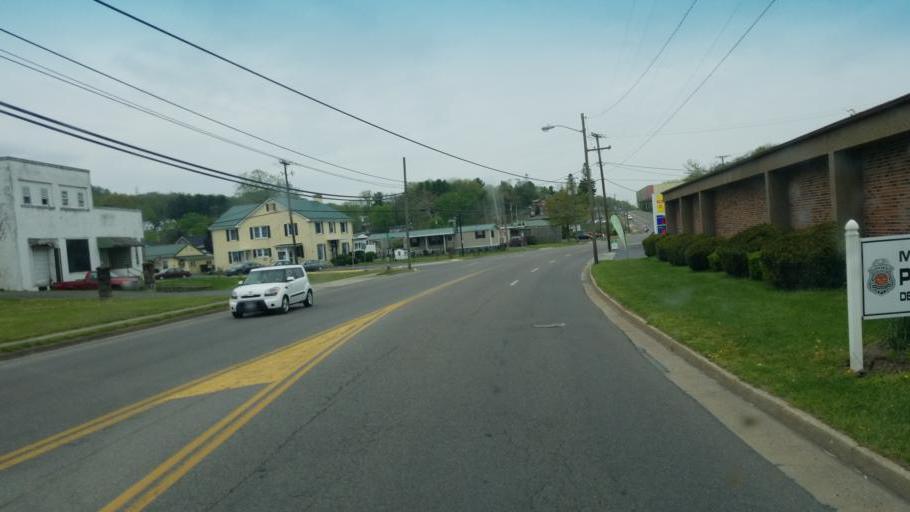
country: US
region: Virginia
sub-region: Smyth County
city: Marion
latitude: 36.8281
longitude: -81.5287
